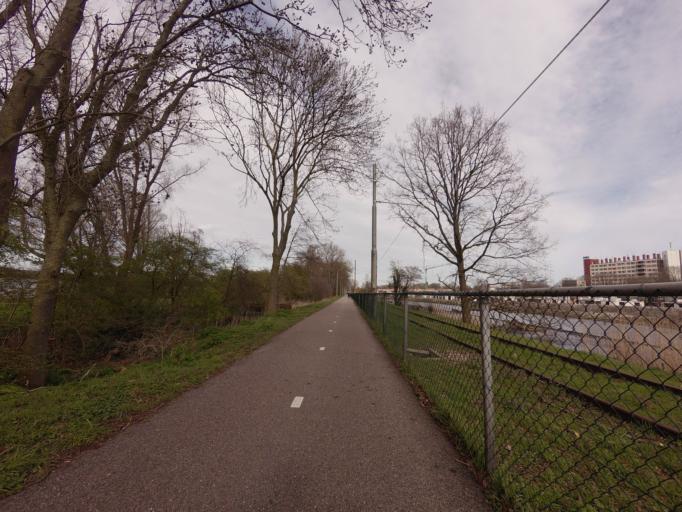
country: NL
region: North Holland
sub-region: Gemeente Amstelveen
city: Amstelveen
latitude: 52.2950
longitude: 4.8419
